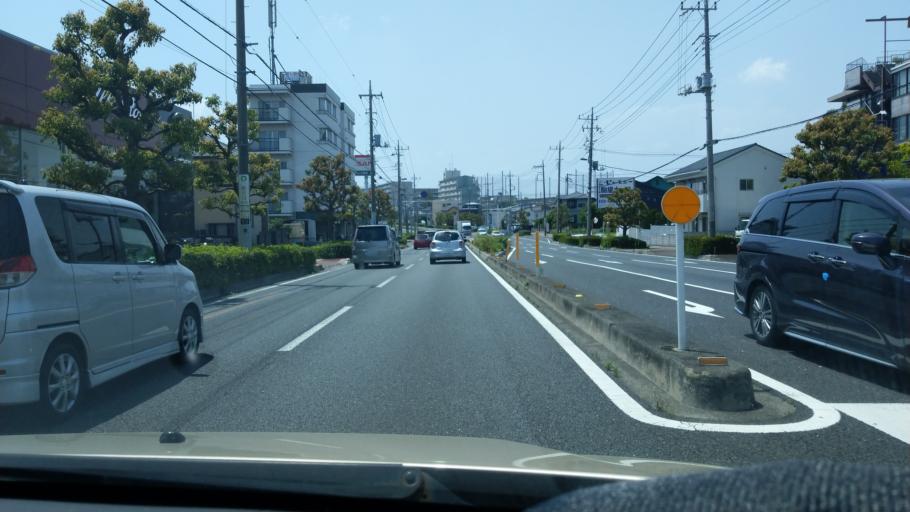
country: JP
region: Saitama
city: Saitama
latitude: 35.8733
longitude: 139.6750
